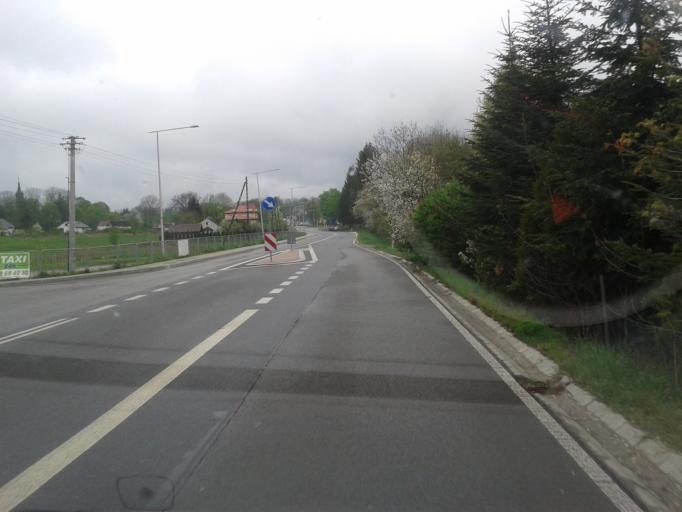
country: PL
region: Lublin Voivodeship
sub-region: Powiat hrubieszowski
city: Dolhobyczow
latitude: 50.5861
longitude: 24.0394
